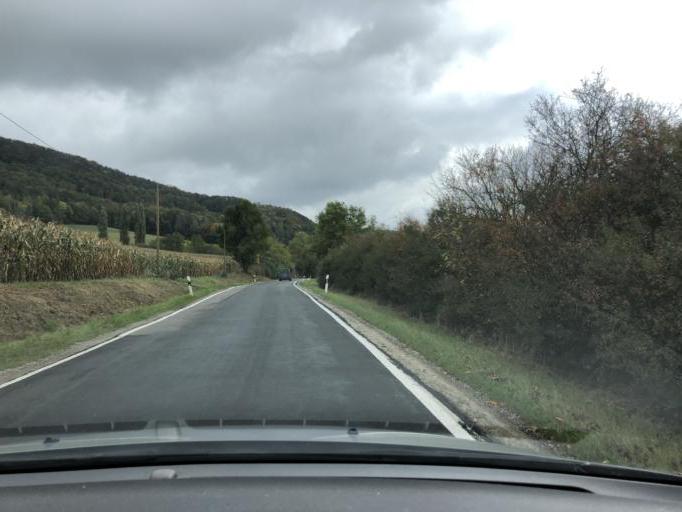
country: DE
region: Thuringia
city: Grossbartloff
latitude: 51.2393
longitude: 10.2063
